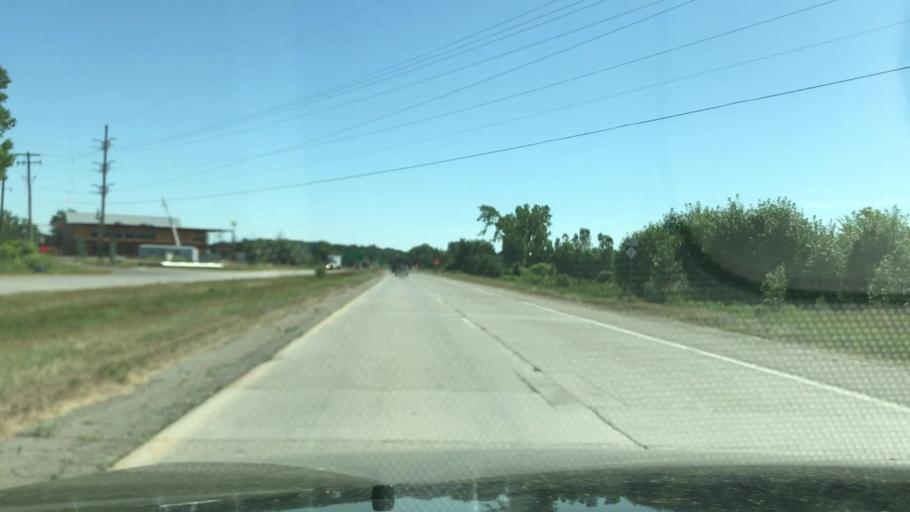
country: US
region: Michigan
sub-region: Ottawa County
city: Zeeland
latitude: 42.8171
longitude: -85.9895
